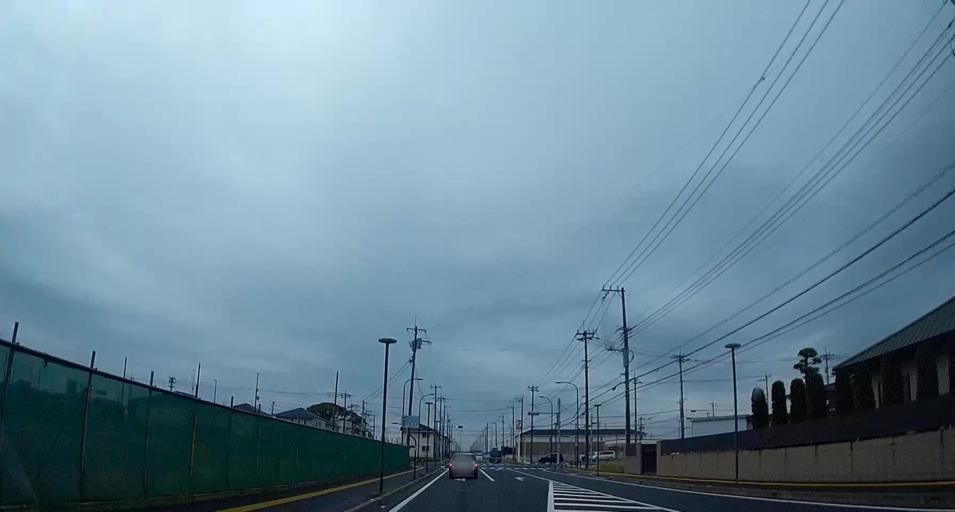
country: JP
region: Chiba
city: Kisarazu
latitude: 35.4330
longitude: 139.9547
